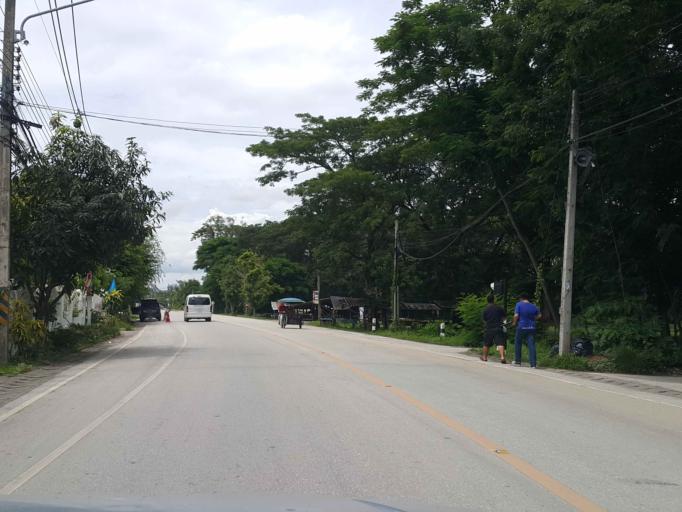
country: TH
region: Chiang Mai
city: San Kamphaeng
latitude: 18.8121
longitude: 99.1211
